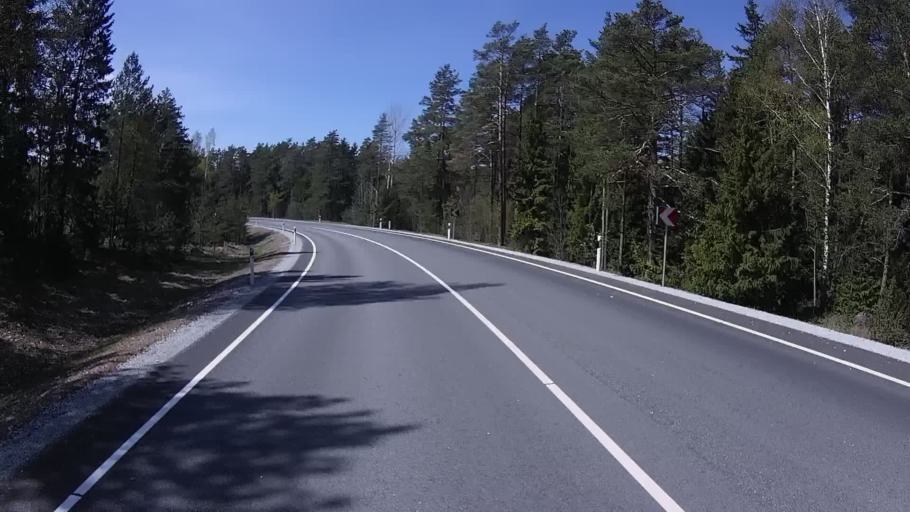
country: EE
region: Laeaene
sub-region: Ridala Parish
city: Uuemoisa
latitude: 59.0419
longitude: 23.8337
